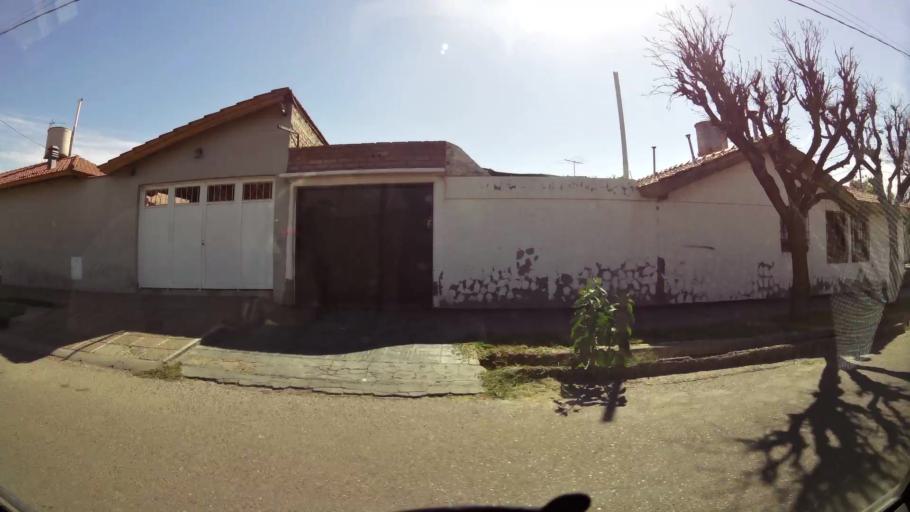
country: AR
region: Mendoza
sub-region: Departamento de Godoy Cruz
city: Godoy Cruz
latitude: -32.9499
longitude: -68.8134
